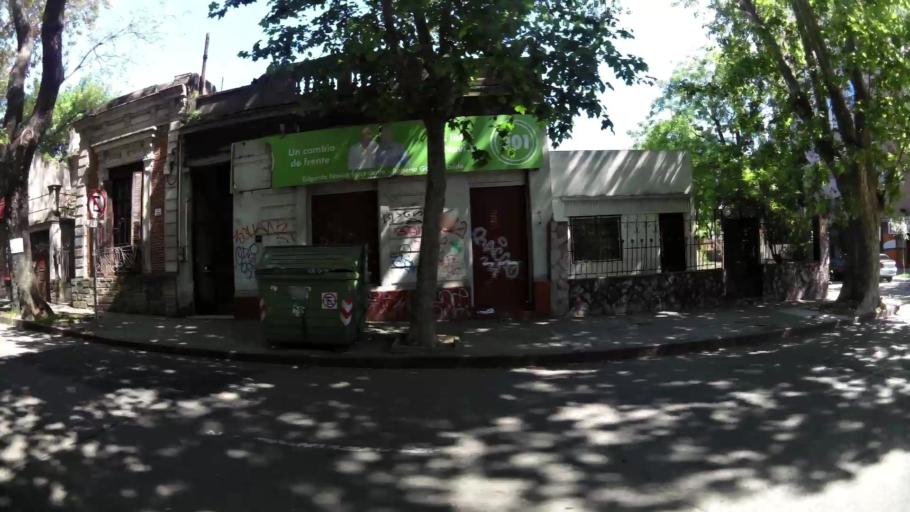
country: UY
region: Montevideo
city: Montevideo
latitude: -34.9030
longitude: -56.1475
